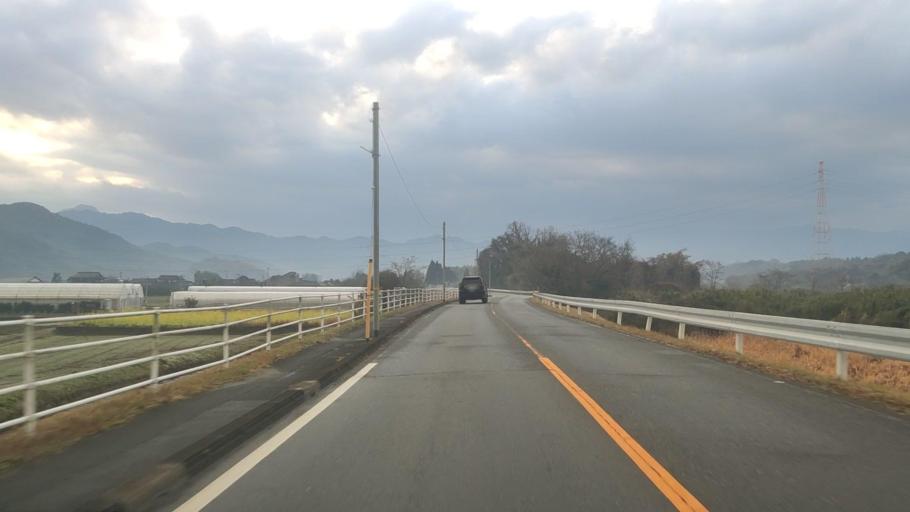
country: JP
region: Kumamoto
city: Uto
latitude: 32.6917
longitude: 130.7922
